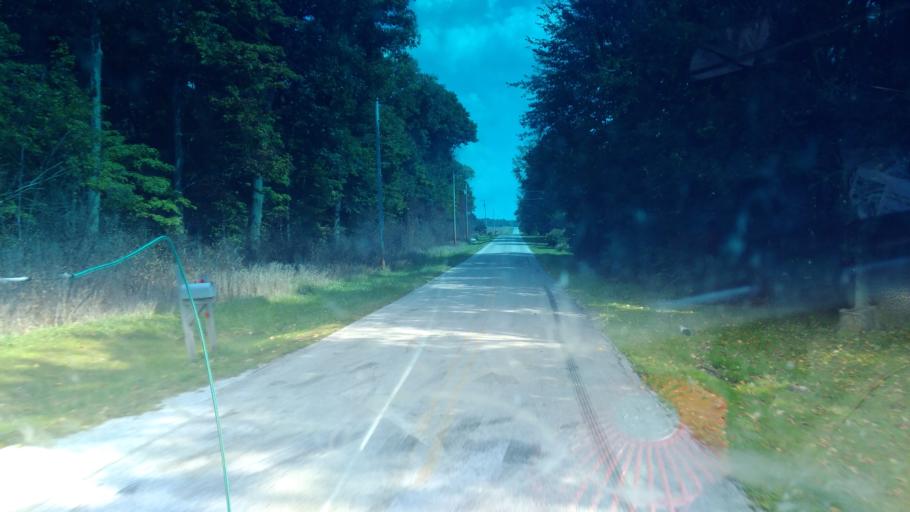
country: US
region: Ohio
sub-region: Hardin County
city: Ada
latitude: 40.7186
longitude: -83.8040
